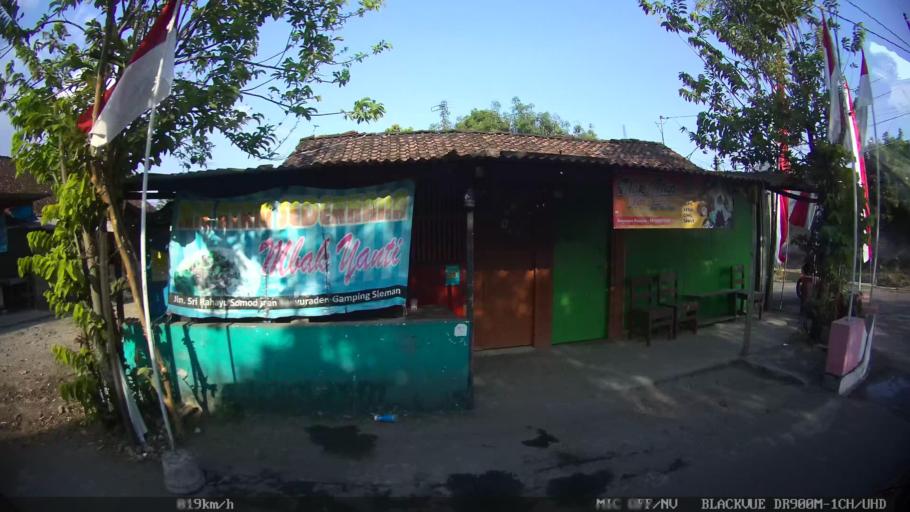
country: ID
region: Daerah Istimewa Yogyakarta
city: Gamping Lor
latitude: -7.7967
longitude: 110.3326
